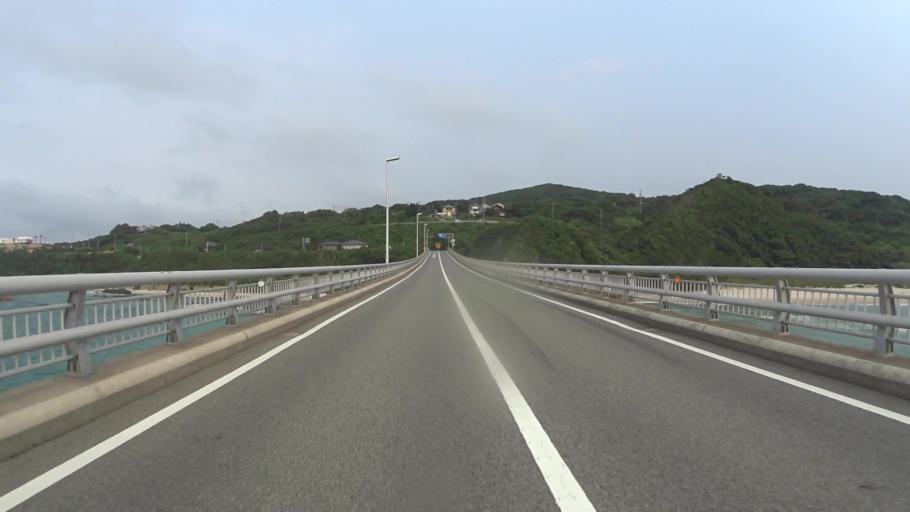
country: JP
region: Yamaguchi
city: Nagato
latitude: 34.3489
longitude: 130.8933
